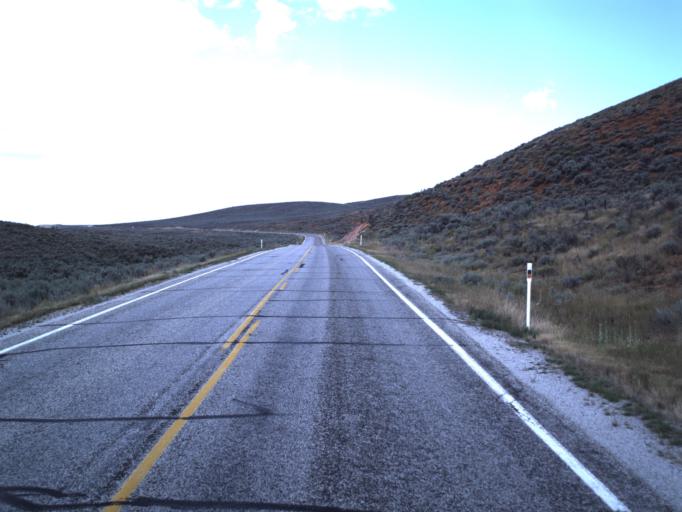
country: US
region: Utah
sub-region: Rich County
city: Randolph
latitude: 41.7882
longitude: -111.2108
